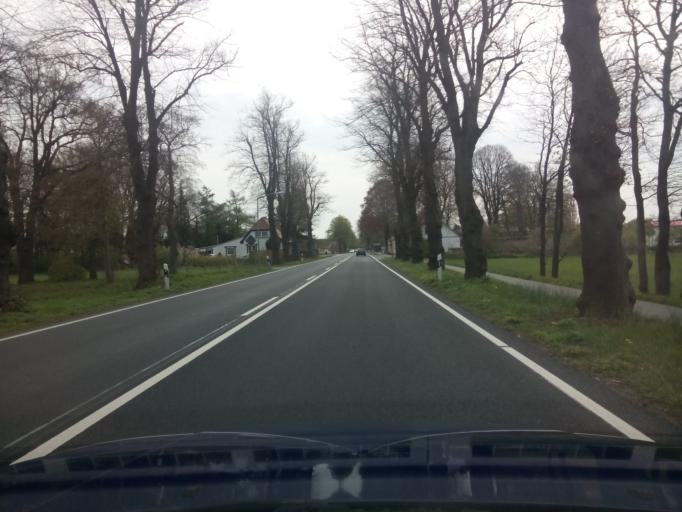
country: DE
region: Lower Saxony
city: Syke
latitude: 52.9722
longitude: 8.7934
